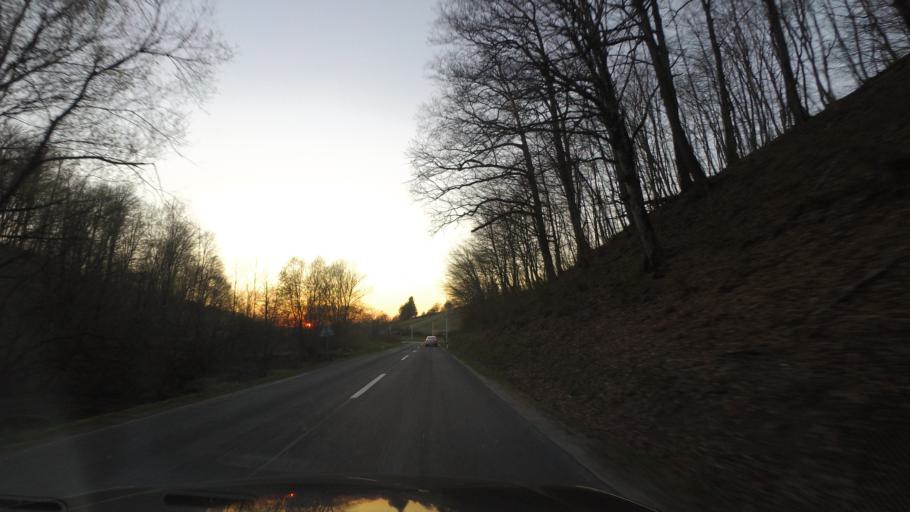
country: HR
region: Karlovacka
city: Vojnic
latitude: 45.3387
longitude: 15.7554
